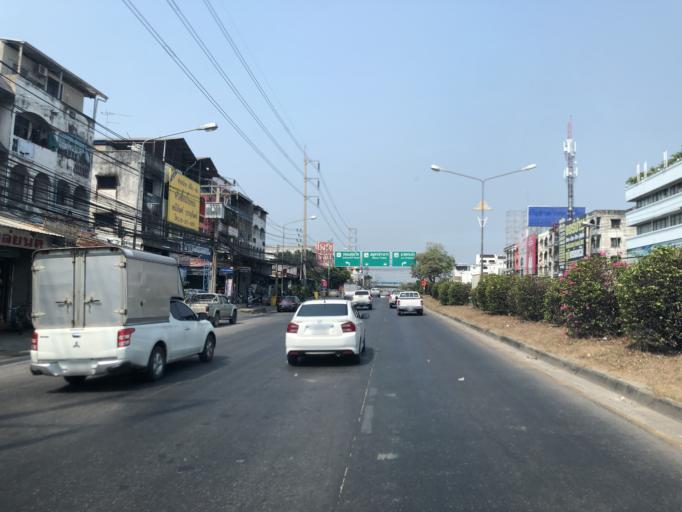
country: TH
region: Bangkok
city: Bang Na
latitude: 13.6030
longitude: 100.7041
